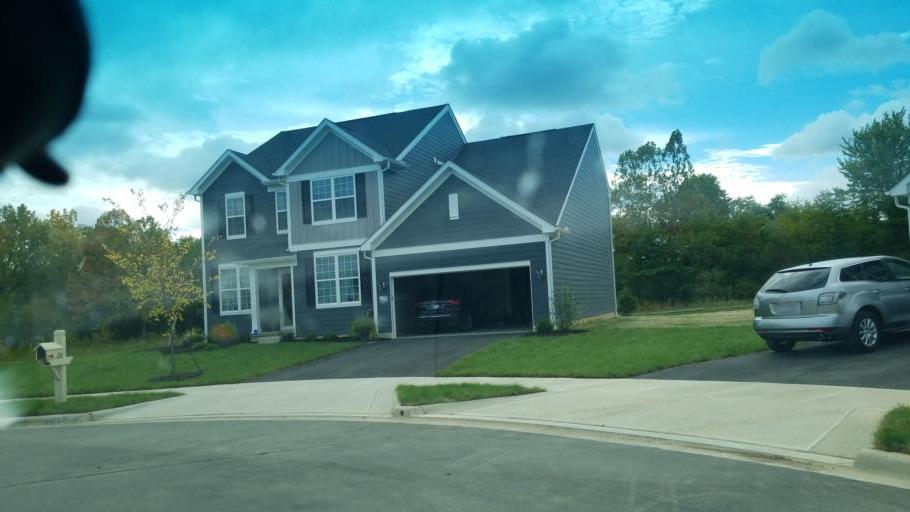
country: US
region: Ohio
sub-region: Delaware County
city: Sunbury
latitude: 40.2375
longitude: -82.8640
